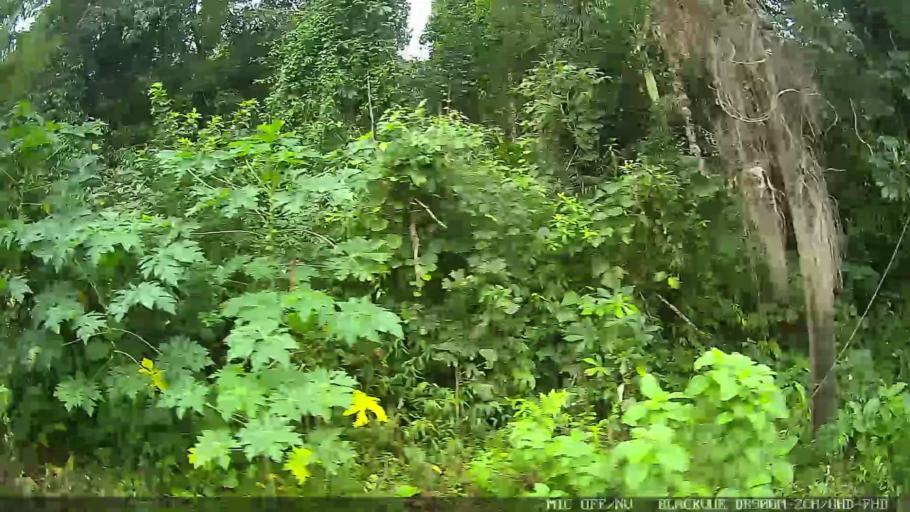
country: BR
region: Sao Paulo
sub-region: Itanhaem
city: Itanhaem
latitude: -24.1923
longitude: -46.8047
